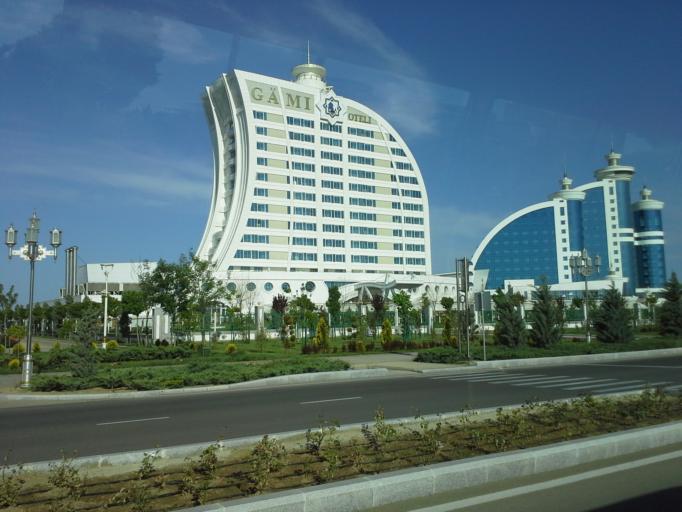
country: TM
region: Balkan
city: Turkmenbasy
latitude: 39.9788
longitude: 52.8277
